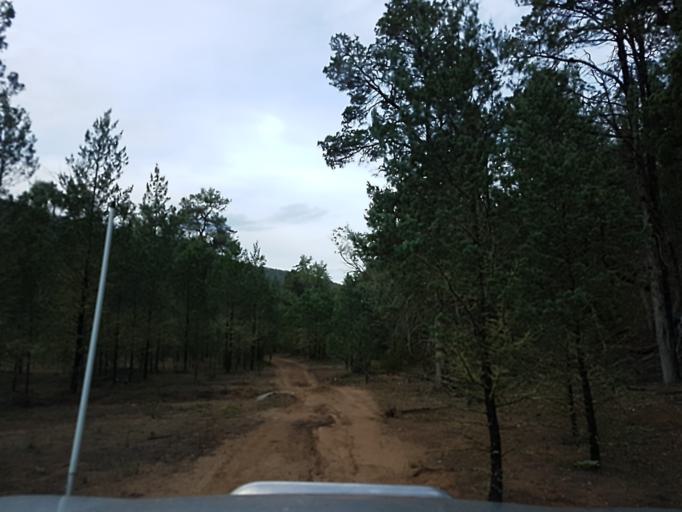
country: AU
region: New South Wales
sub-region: Snowy River
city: Jindabyne
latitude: -36.9462
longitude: 148.3825
